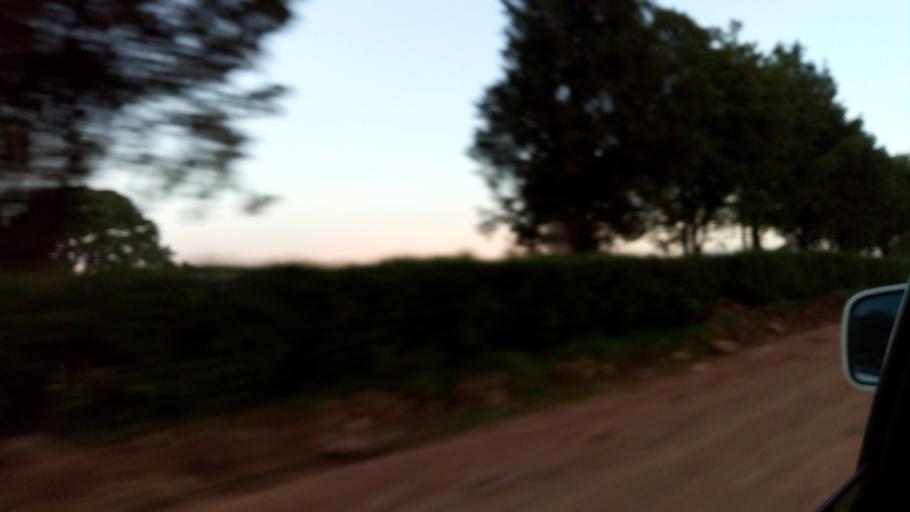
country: KE
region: Nyamira District
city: Nyamira
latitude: -0.5825
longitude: 35.0509
